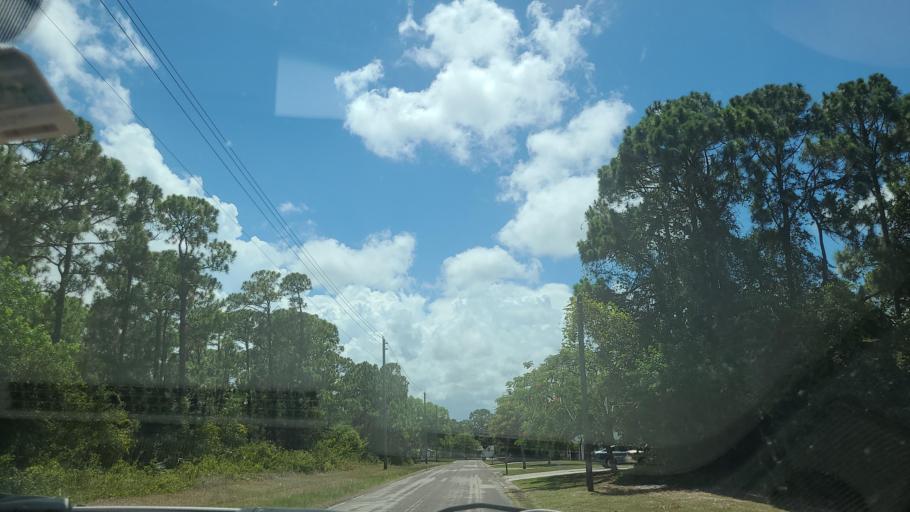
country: US
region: Florida
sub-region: Indian River County
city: Sebastian
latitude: 27.7728
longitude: -80.4672
